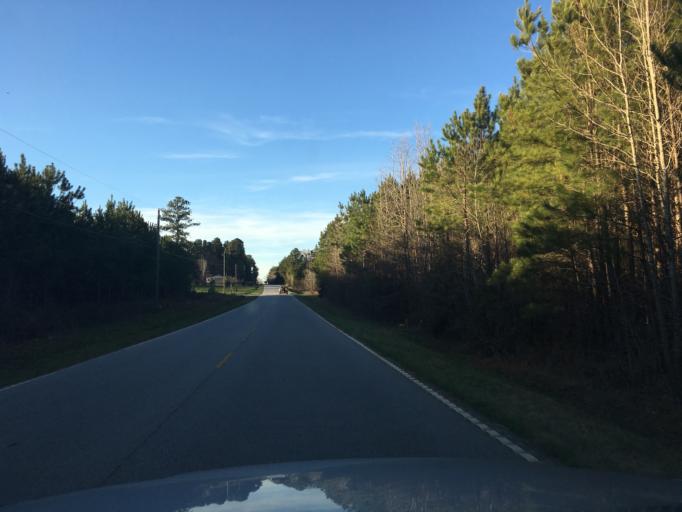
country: US
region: South Carolina
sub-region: Saluda County
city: Saluda
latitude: 34.0746
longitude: -81.8197
